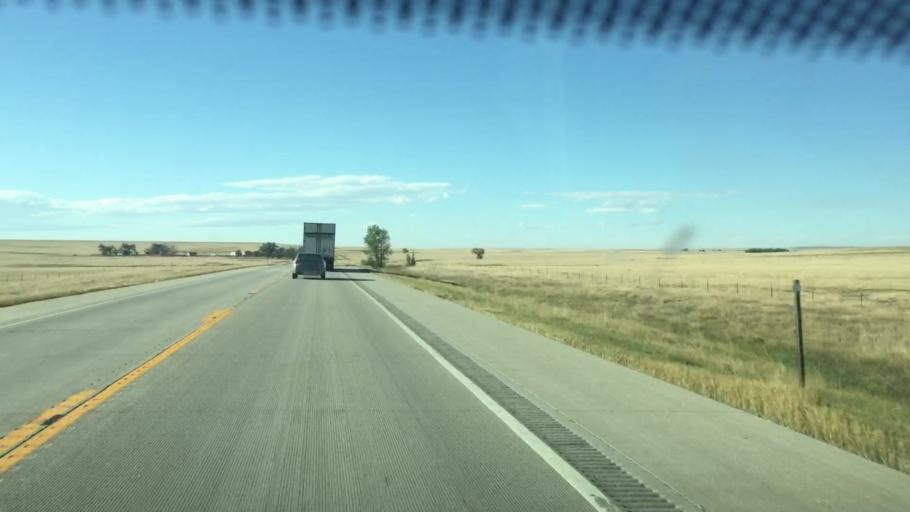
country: US
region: Colorado
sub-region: Lincoln County
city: Hugo
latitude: 38.9299
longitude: -103.1968
